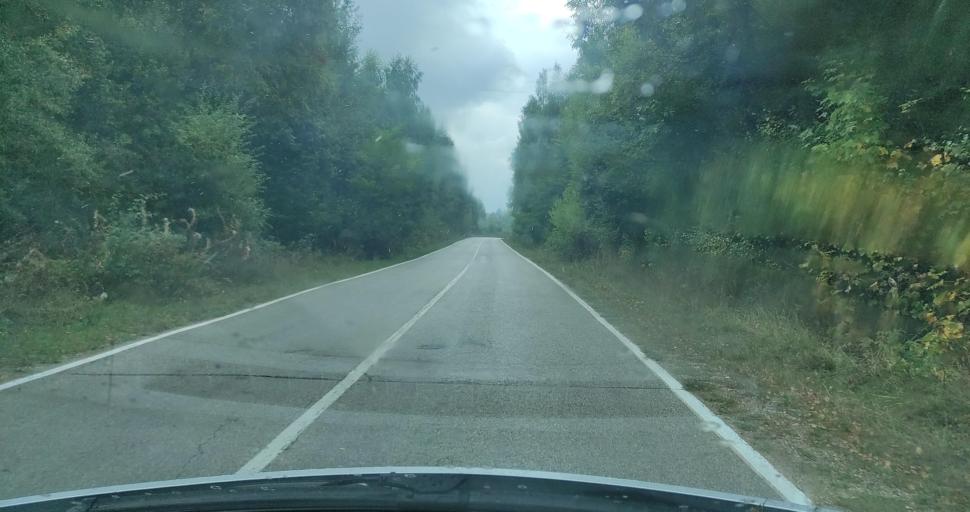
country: RS
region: Central Serbia
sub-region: Jablanicki Okrug
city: Crna Trava
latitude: 42.7147
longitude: 22.3288
